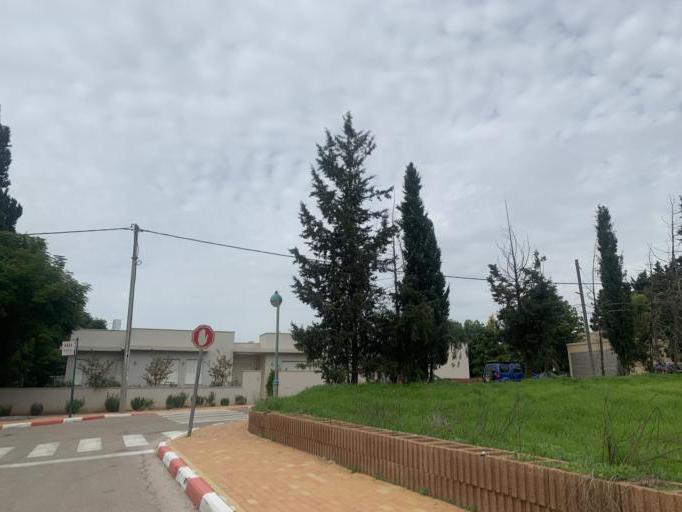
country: IL
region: Central District
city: Hod HaSharon
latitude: 32.1696
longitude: 34.8880
